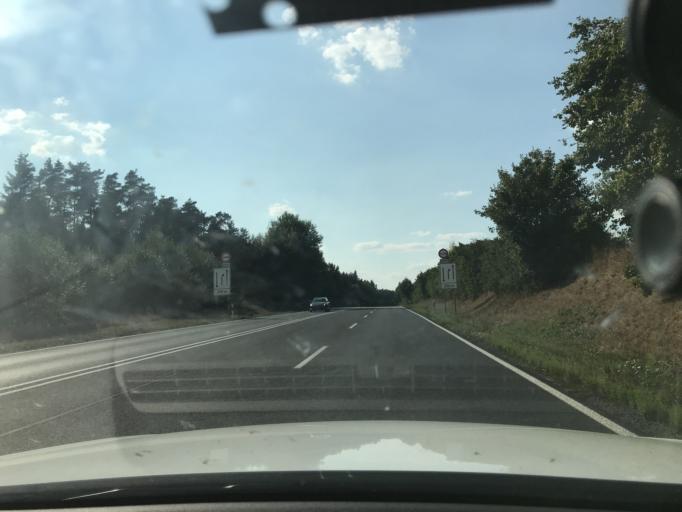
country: DE
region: Bavaria
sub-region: Upper Palatinate
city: Poppenricht
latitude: 49.4659
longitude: 11.7782
